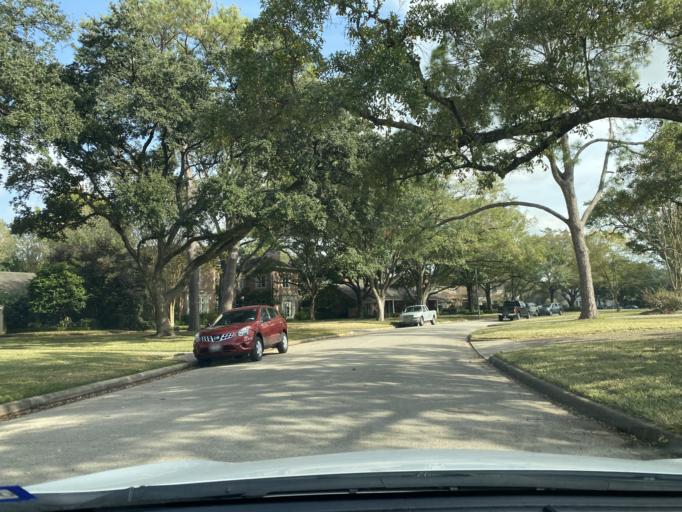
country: US
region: Texas
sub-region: Harris County
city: Hunters Creek Village
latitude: 29.7621
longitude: -95.4749
